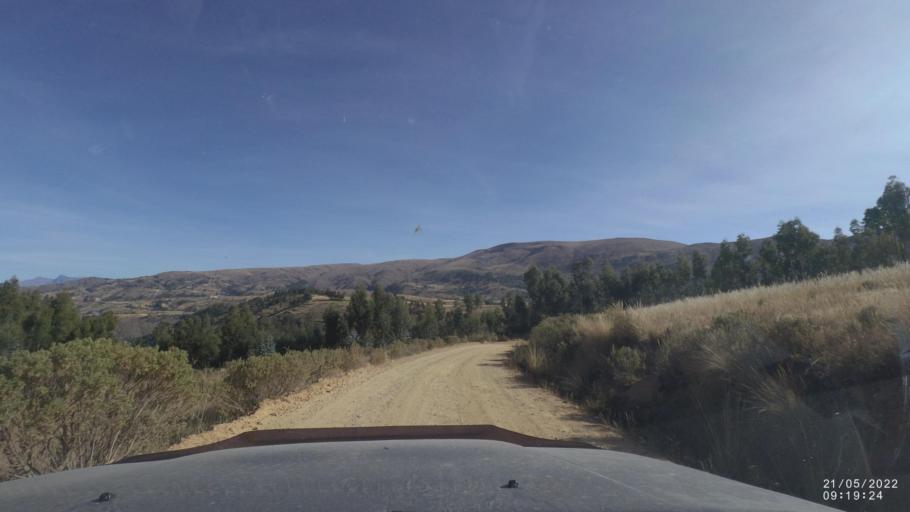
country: BO
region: Cochabamba
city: Cochabamba
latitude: -17.3577
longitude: -66.0204
